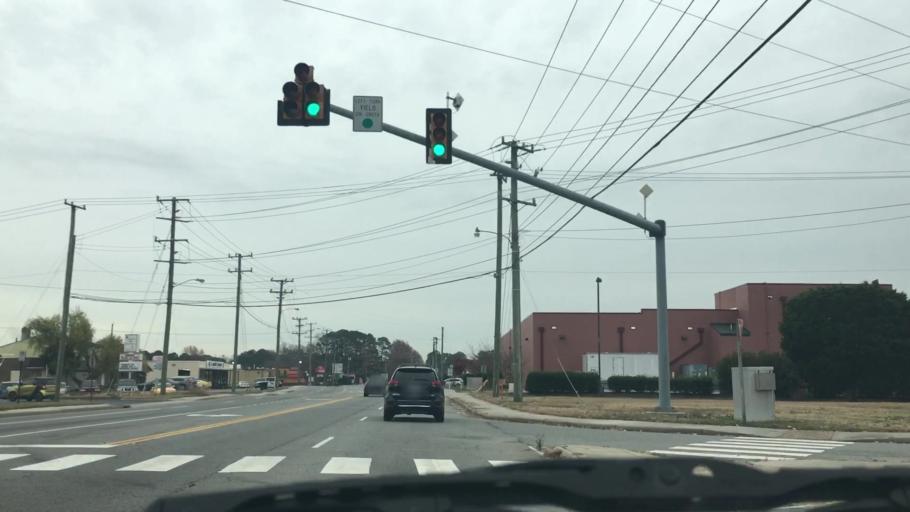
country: US
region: Virginia
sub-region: City of Portsmouth
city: Portsmouth Heights
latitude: 36.8633
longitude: -76.3950
